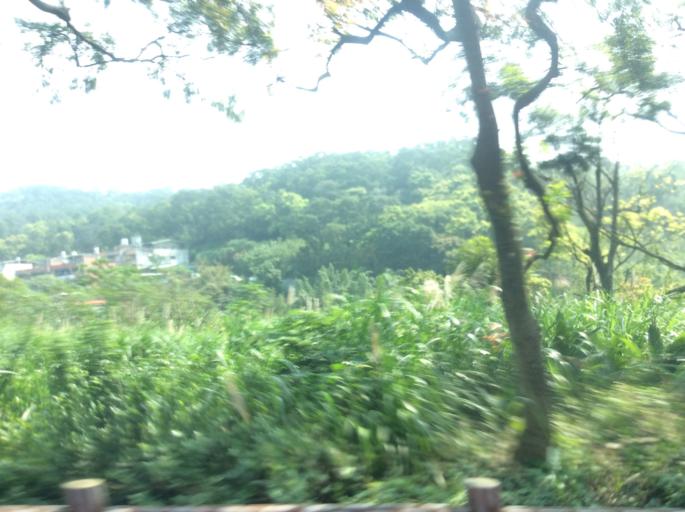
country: TW
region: Taipei
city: Taipei
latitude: 25.1274
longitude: 121.5489
